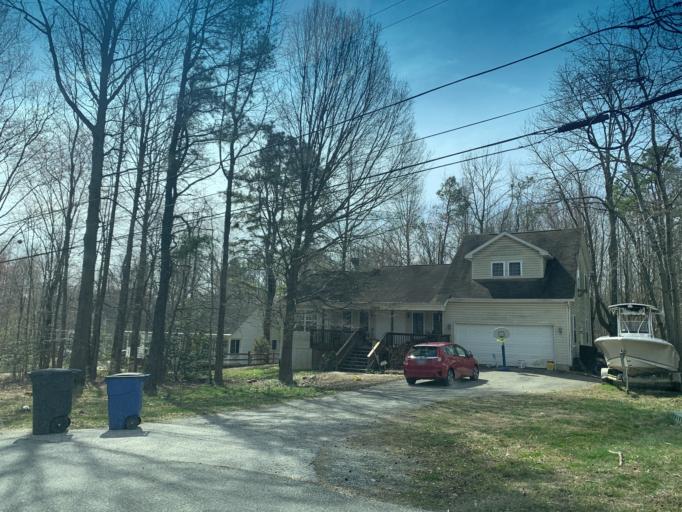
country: US
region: Maryland
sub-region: Cecil County
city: Charlestown
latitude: 39.5774
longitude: -75.9810
